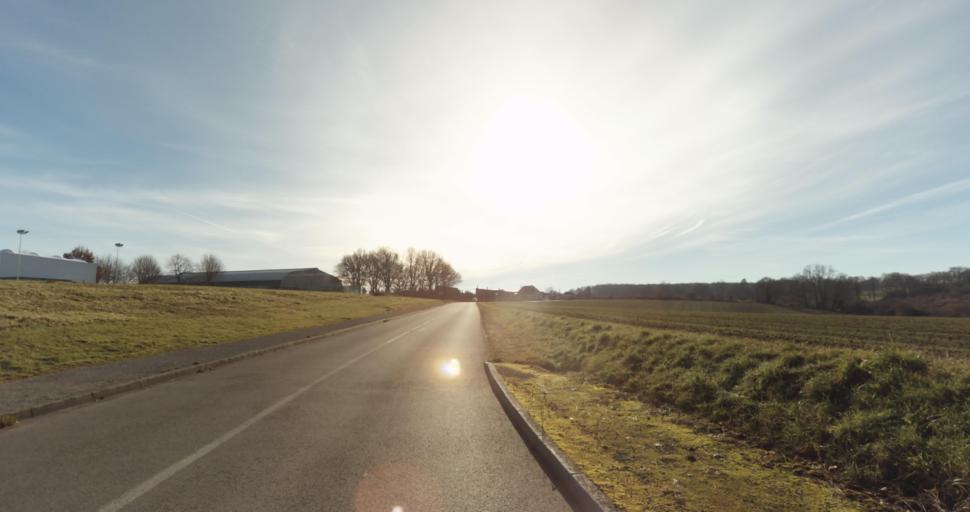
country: FR
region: Limousin
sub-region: Departement de la Haute-Vienne
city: Aixe-sur-Vienne
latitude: 45.7920
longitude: 1.1302
